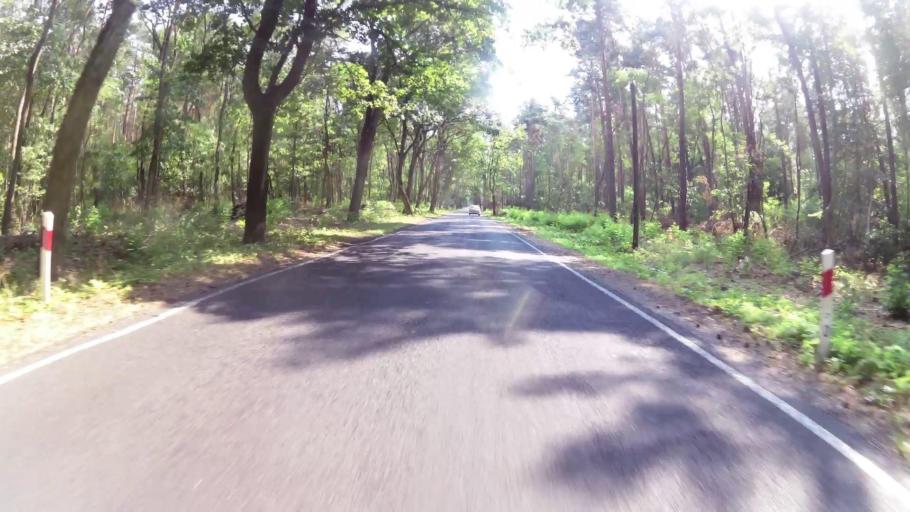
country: PL
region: West Pomeranian Voivodeship
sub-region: Powiat gryfinski
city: Moryn
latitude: 52.8365
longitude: 14.4098
